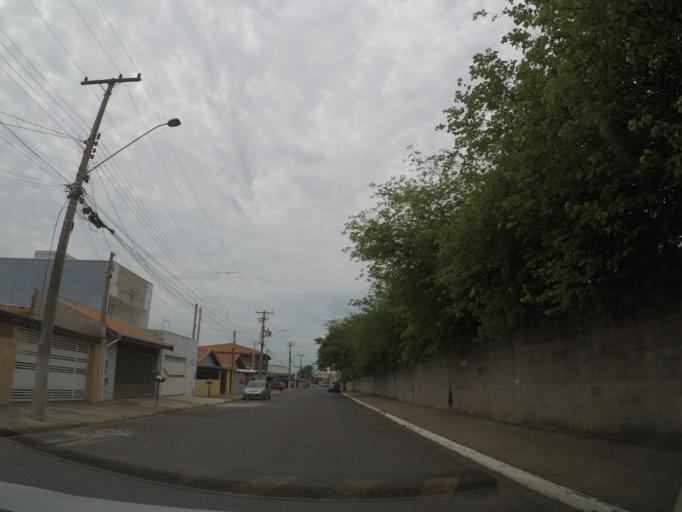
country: BR
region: Sao Paulo
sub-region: Hortolandia
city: Hortolandia
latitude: -22.8356
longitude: -47.1927
